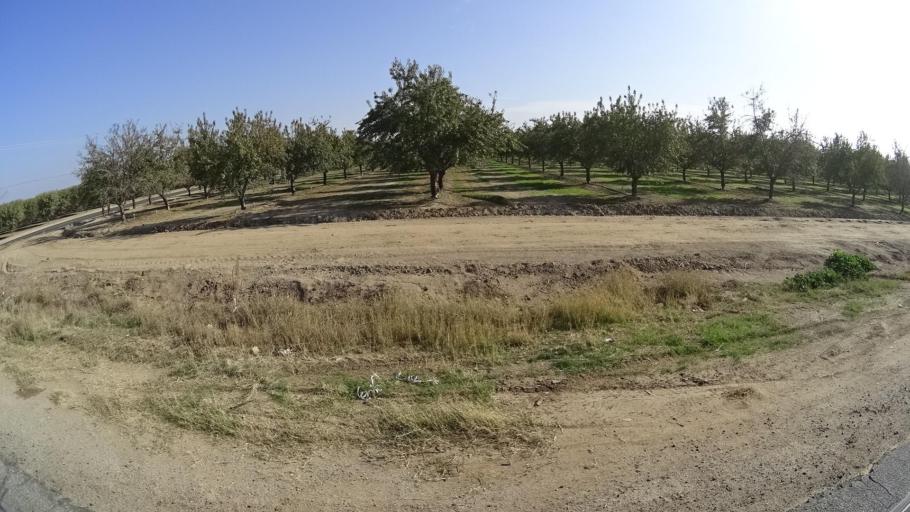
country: US
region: California
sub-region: Kern County
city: McFarland
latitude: 35.6888
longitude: -119.2048
